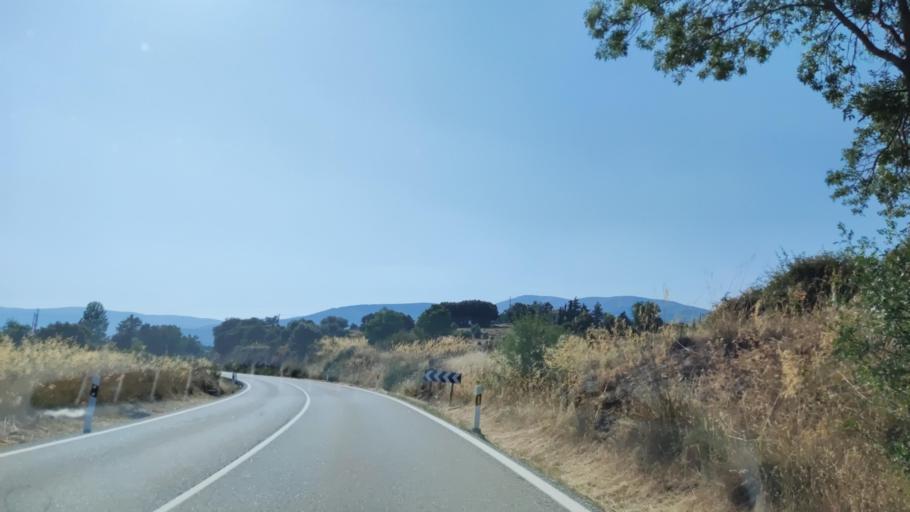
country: ES
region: Madrid
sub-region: Provincia de Madrid
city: Lozoya
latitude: 40.9481
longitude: -3.7643
